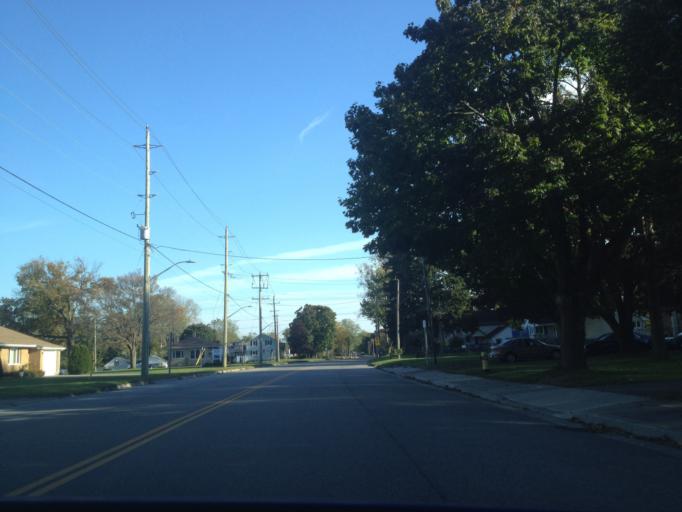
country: CA
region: Ontario
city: Delaware
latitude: 42.5969
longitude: -81.5979
